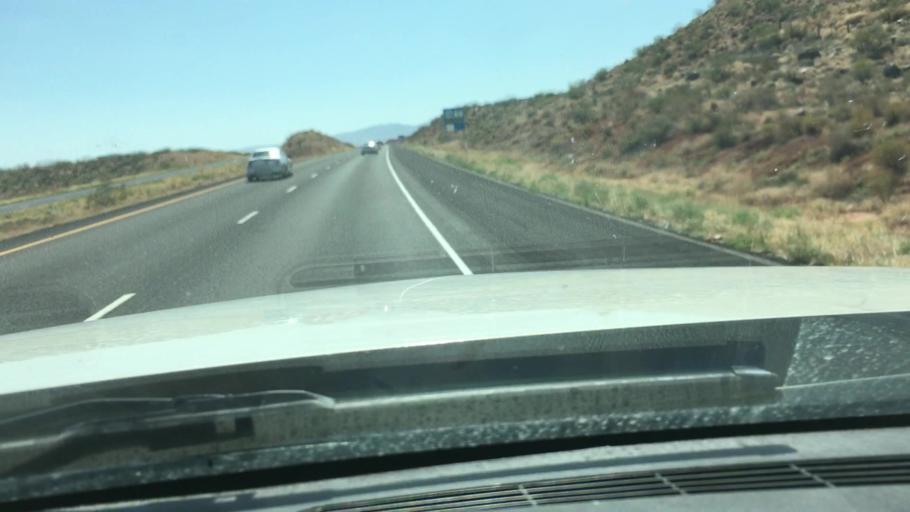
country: US
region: Utah
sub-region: Washington County
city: Washington
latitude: 37.1774
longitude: -113.4250
